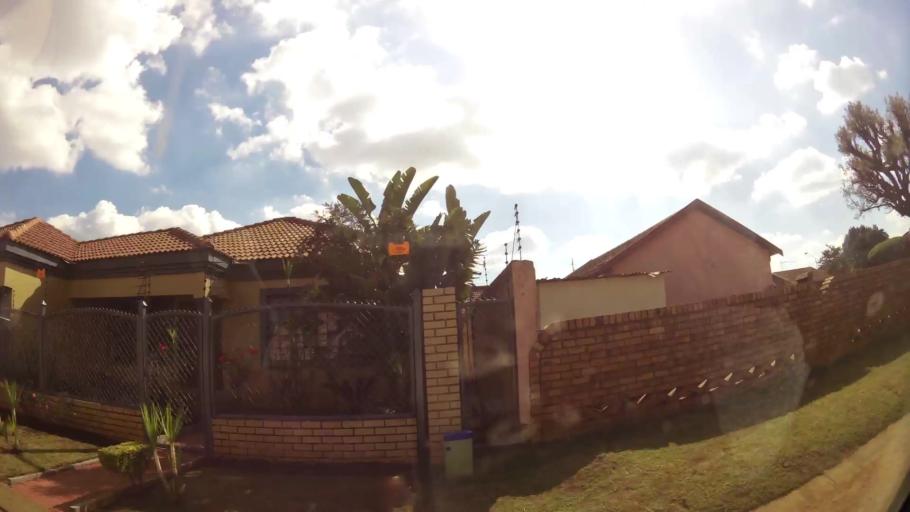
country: ZA
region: Gauteng
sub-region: City of Tshwane Metropolitan Municipality
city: Cullinan
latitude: -25.7029
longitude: 28.4164
